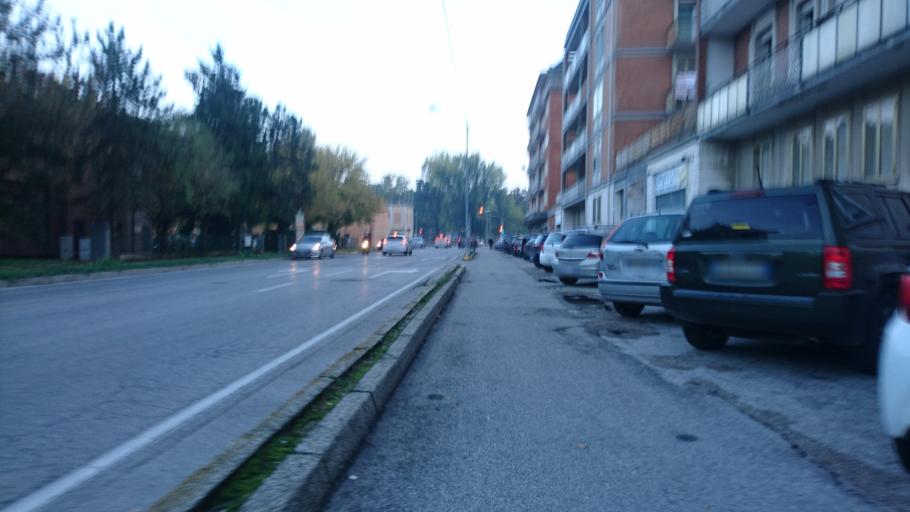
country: IT
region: Emilia-Romagna
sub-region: Provincia di Ferrara
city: Ferrara
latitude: 44.8518
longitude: 11.6153
